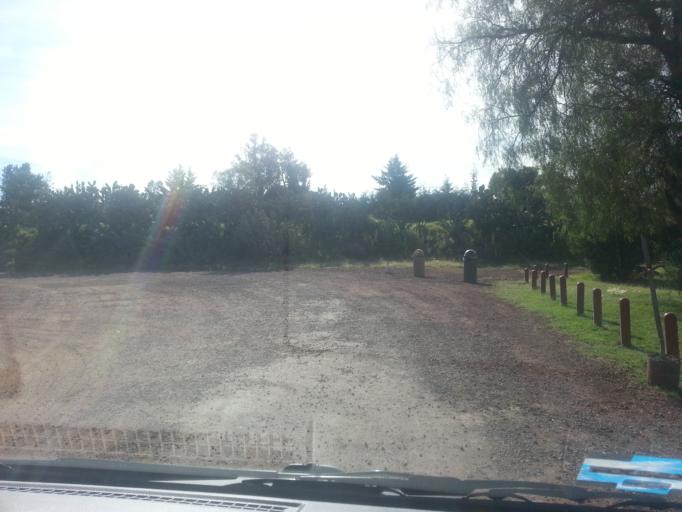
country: MX
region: Mexico
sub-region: Teotihuacan
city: Teotihuacan de Arista
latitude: 19.6829
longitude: -98.8508
